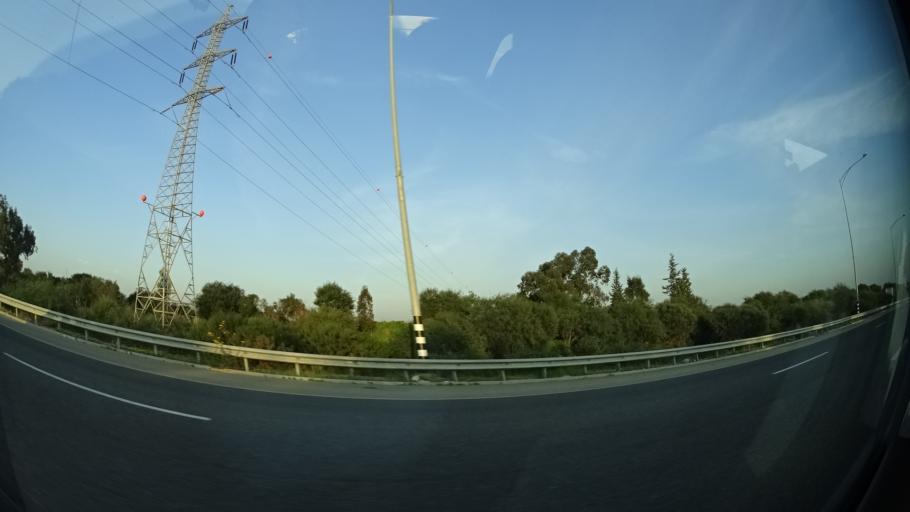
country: IL
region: Central District
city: Kefar Habad
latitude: 31.9943
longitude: 34.8555
